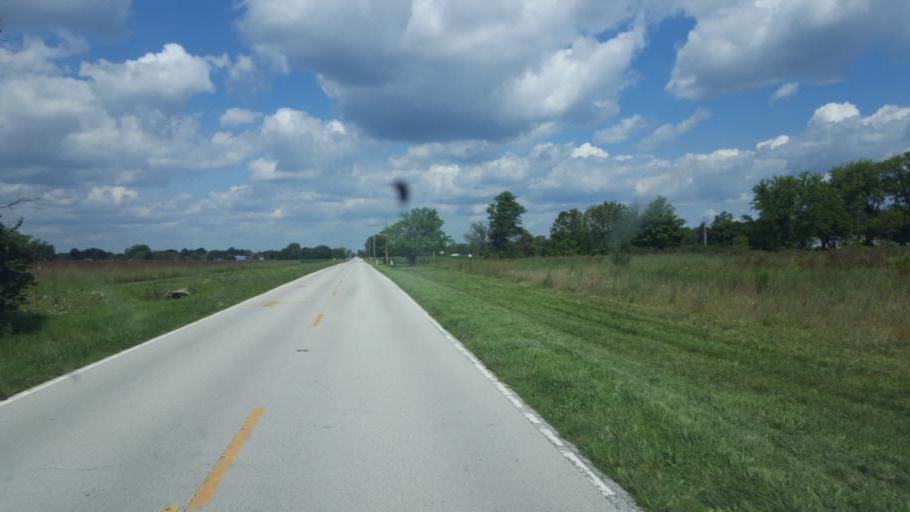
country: US
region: Ohio
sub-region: Sandusky County
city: Gibsonburg
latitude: 41.3772
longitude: -83.3006
